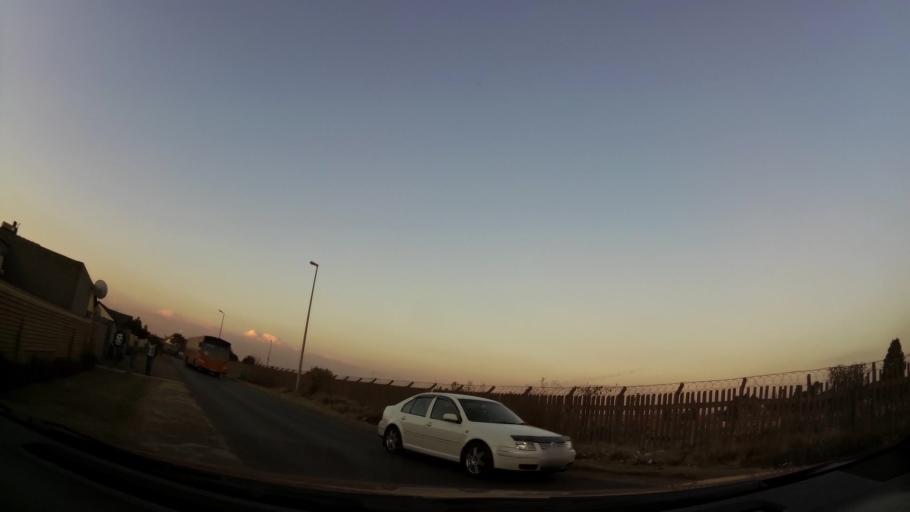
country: ZA
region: Gauteng
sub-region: City of Johannesburg Metropolitan Municipality
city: Soweto
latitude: -26.2267
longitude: 27.8439
